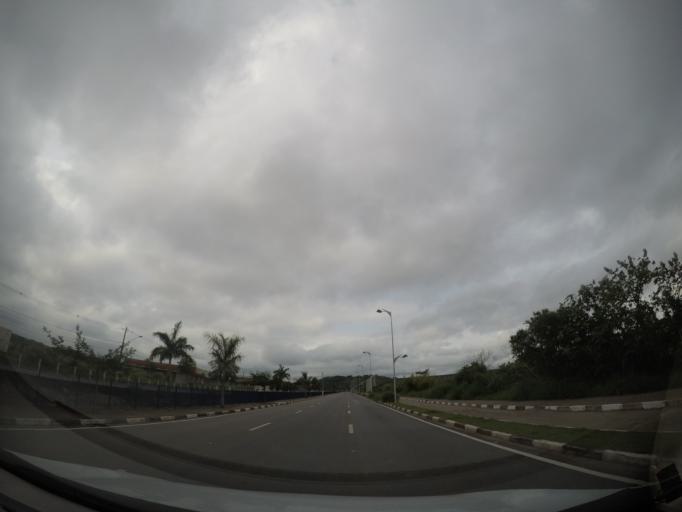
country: BR
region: Sao Paulo
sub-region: Aruja
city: Aruja
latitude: -23.4088
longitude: -46.3658
